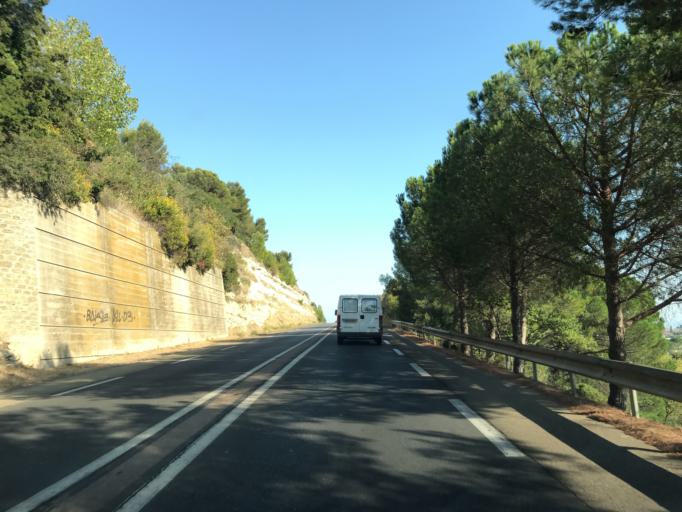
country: FR
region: Provence-Alpes-Cote d'Azur
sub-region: Departement des Bouches-du-Rhone
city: Saint-Chamas
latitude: 43.5532
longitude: 5.0353
